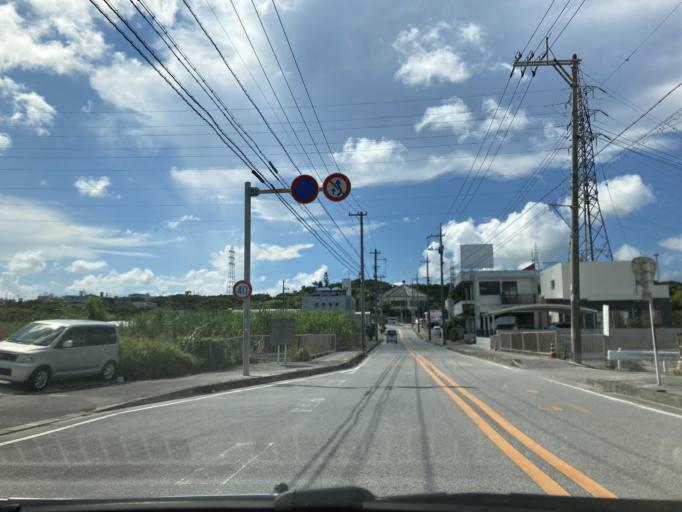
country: JP
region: Okinawa
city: Tomigusuku
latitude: 26.1682
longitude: 127.7205
